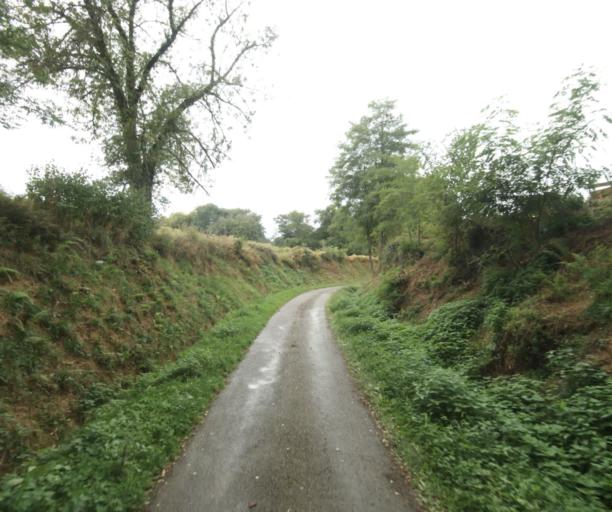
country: FR
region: Midi-Pyrenees
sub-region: Departement du Gers
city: Cazaubon
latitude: 43.8956
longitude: -0.1097
